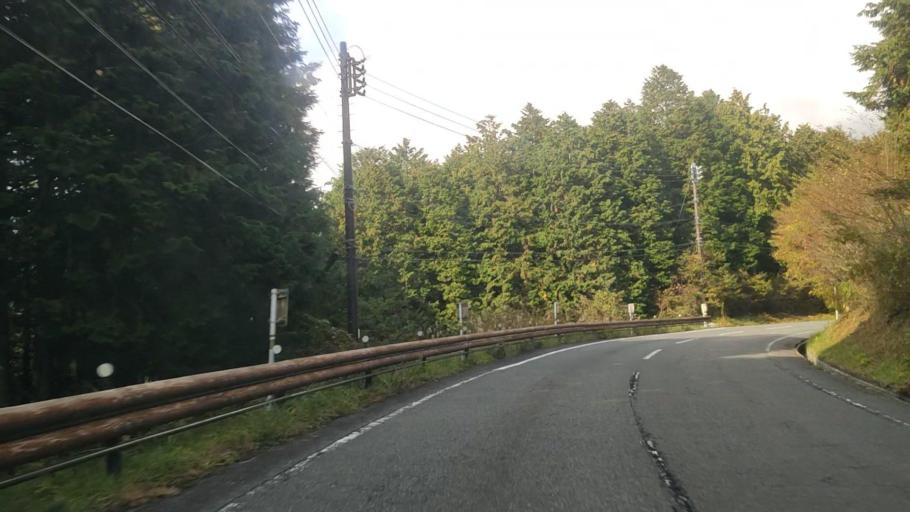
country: JP
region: Shizuoka
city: Fujinomiya
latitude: 35.2982
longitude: 138.6689
